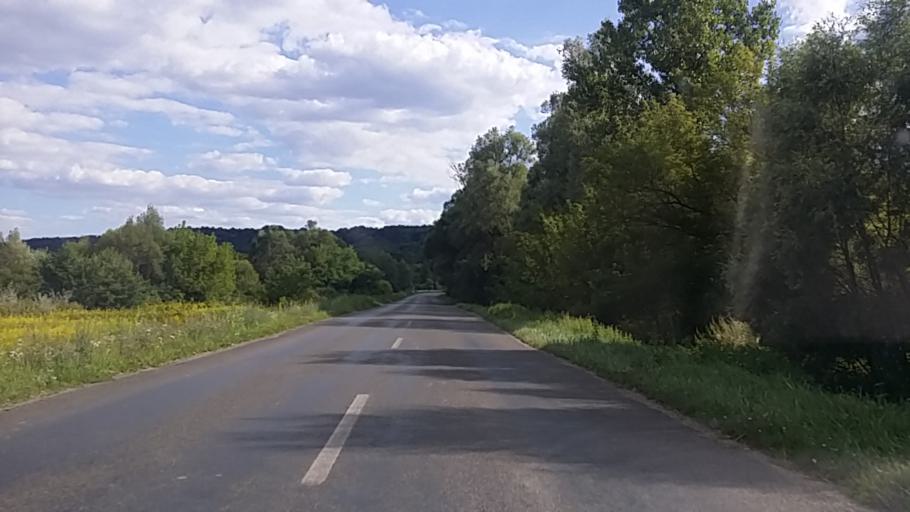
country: HU
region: Baranya
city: Sasd
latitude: 46.2135
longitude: 18.1043
